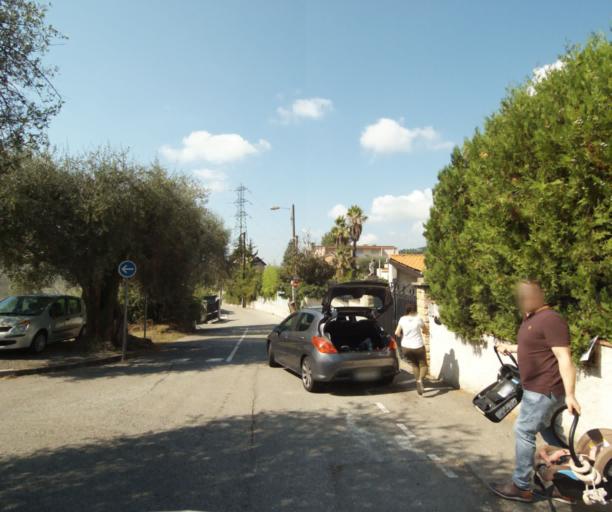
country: FR
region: Provence-Alpes-Cote d'Azur
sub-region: Departement des Alpes-Maritimes
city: Drap
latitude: 43.7469
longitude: 7.3226
